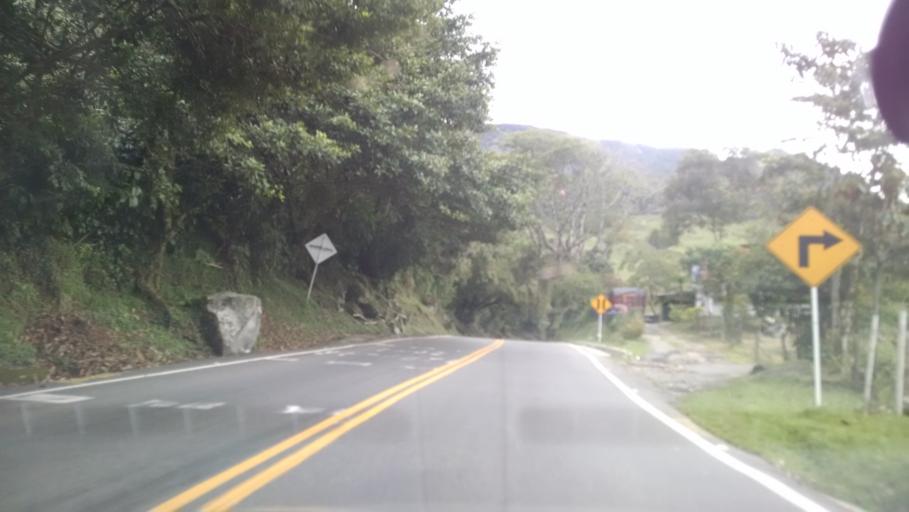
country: CO
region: Antioquia
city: Cocorna
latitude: 6.0255
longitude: -75.1689
